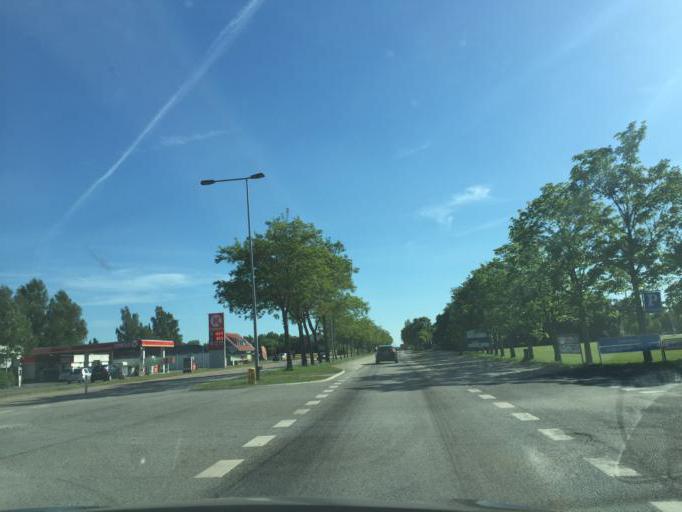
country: DK
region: Zealand
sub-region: Koge Kommune
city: Koge
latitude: 55.4148
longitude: 12.1387
